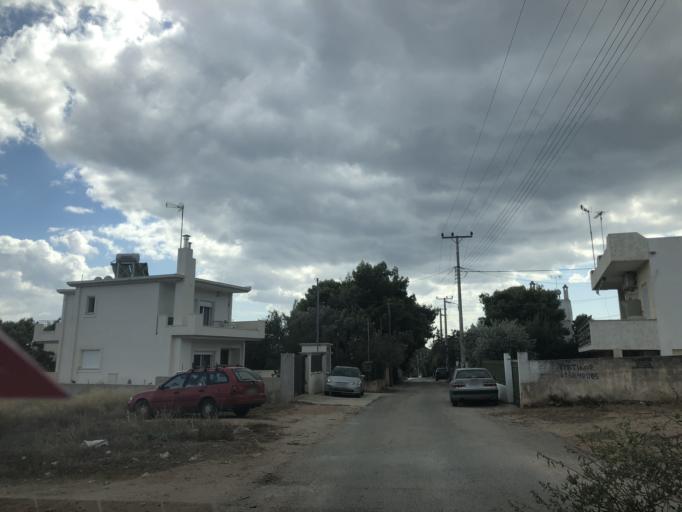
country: GR
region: Attica
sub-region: Nomarchia Anatolikis Attikis
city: Agia Marina
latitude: 37.8253
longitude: 23.8442
